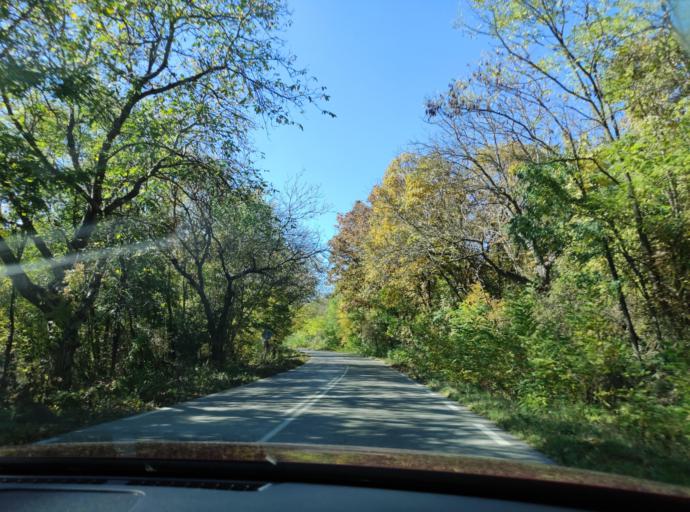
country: BG
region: Montana
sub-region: Obshtina Montana
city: Montana
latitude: 43.4074
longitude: 23.0608
